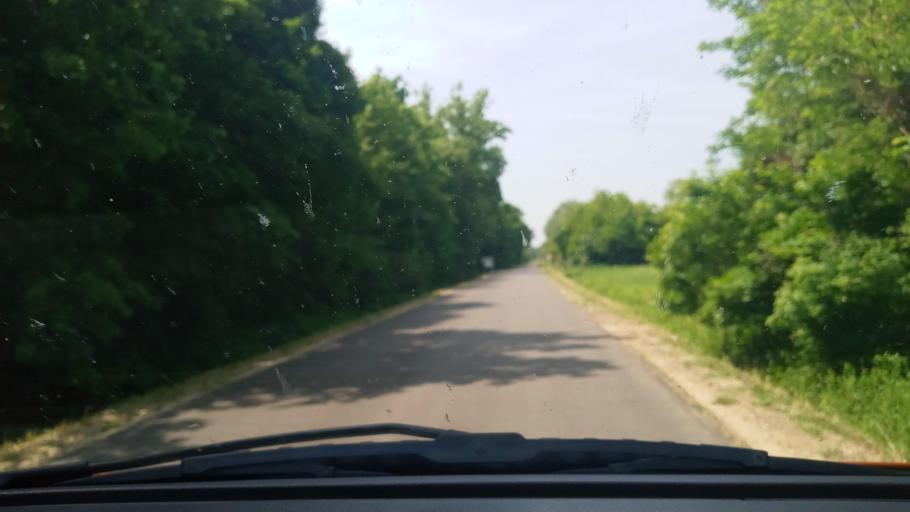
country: HU
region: Somogy
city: Barcs
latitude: 45.9567
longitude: 17.6428
